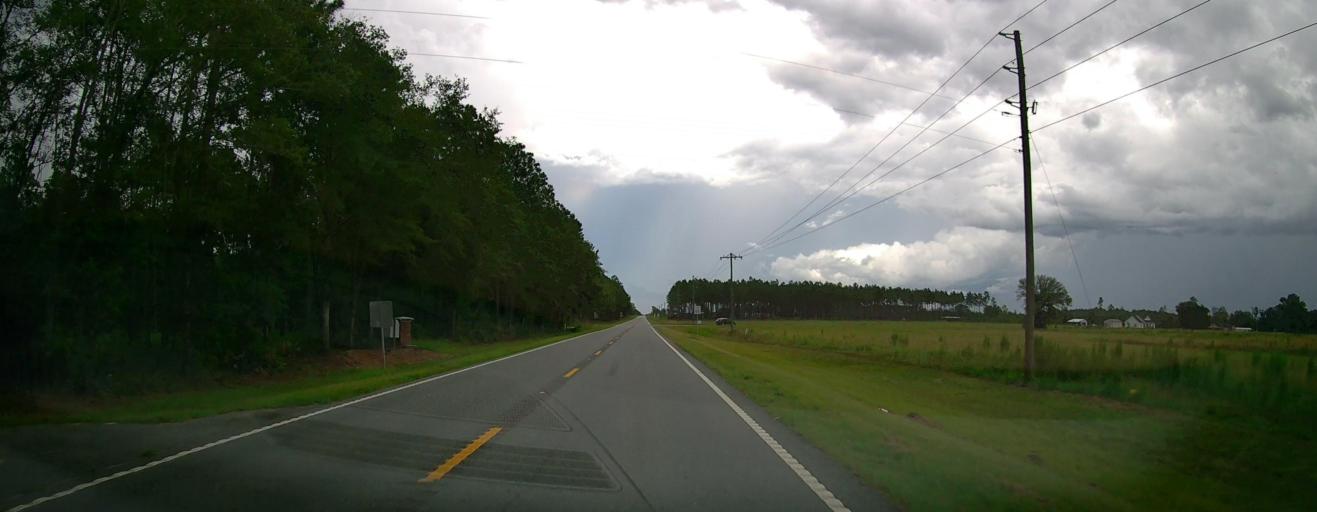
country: US
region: Georgia
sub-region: Pierce County
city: Blackshear
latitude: 31.3763
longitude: -82.1205
